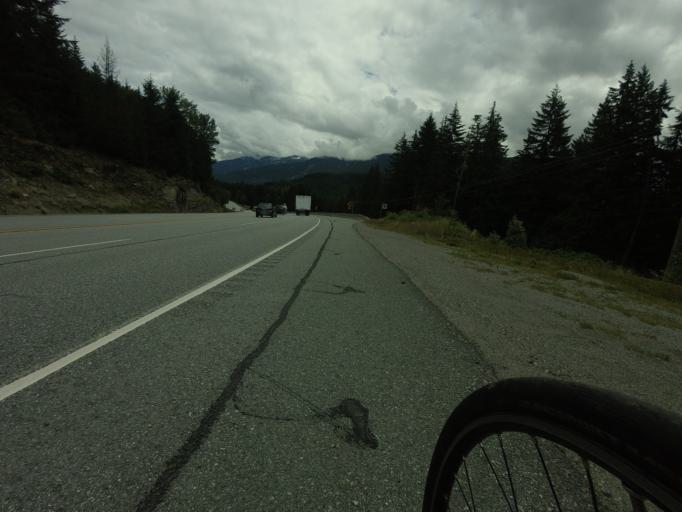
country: CA
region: British Columbia
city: Whistler
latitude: 50.0832
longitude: -123.0570
